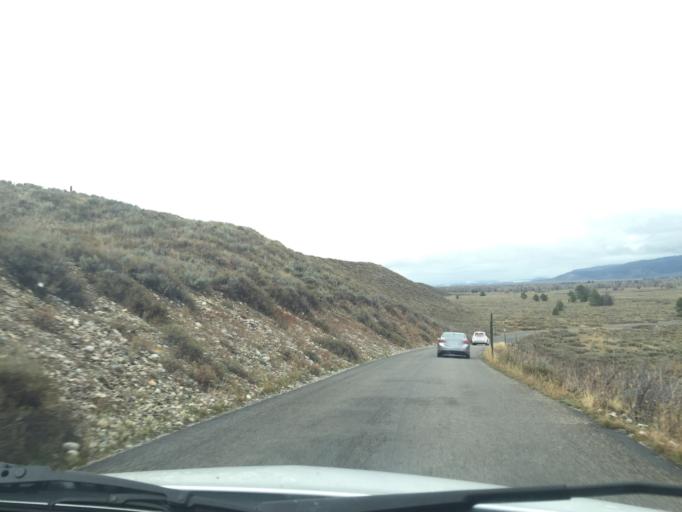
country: US
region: Wyoming
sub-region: Teton County
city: Moose Wilson Road
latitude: 43.6592
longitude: -110.7309
